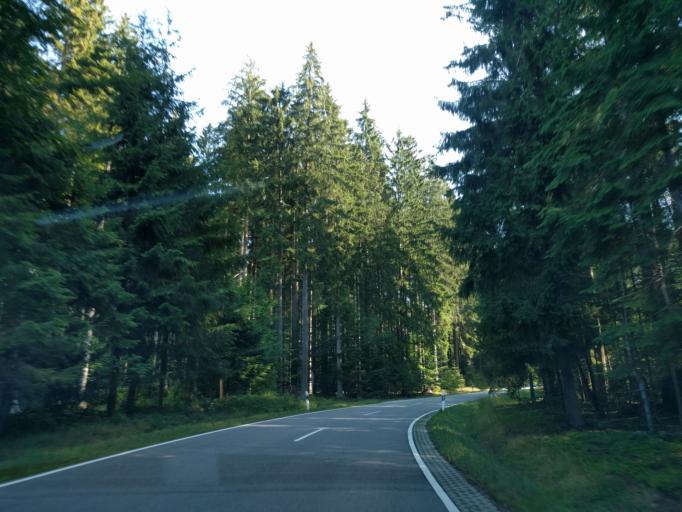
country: DE
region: Bavaria
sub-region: Lower Bavaria
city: Mauth
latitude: 48.8704
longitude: 13.5481
